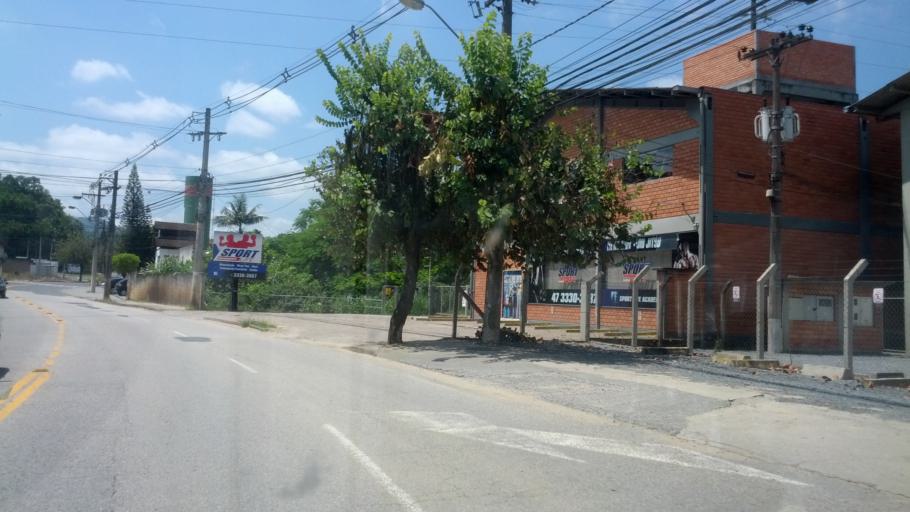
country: BR
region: Santa Catarina
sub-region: Blumenau
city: Blumenau
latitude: -26.9004
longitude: -49.1353
